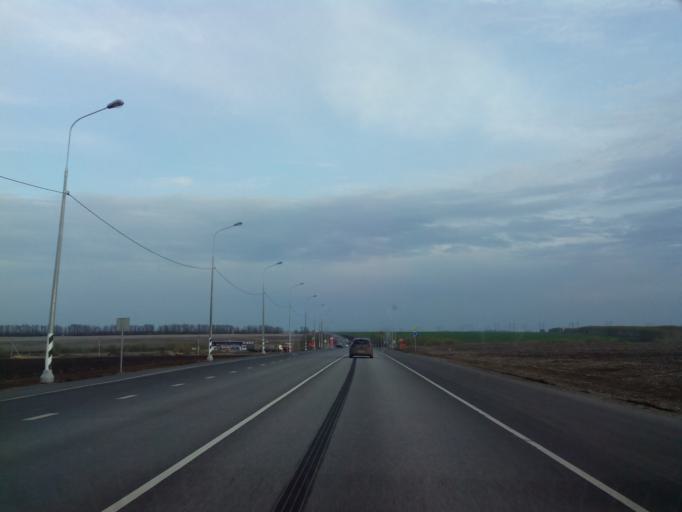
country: RU
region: Rjazan
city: Ryazhsk
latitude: 53.5606
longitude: 40.0515
